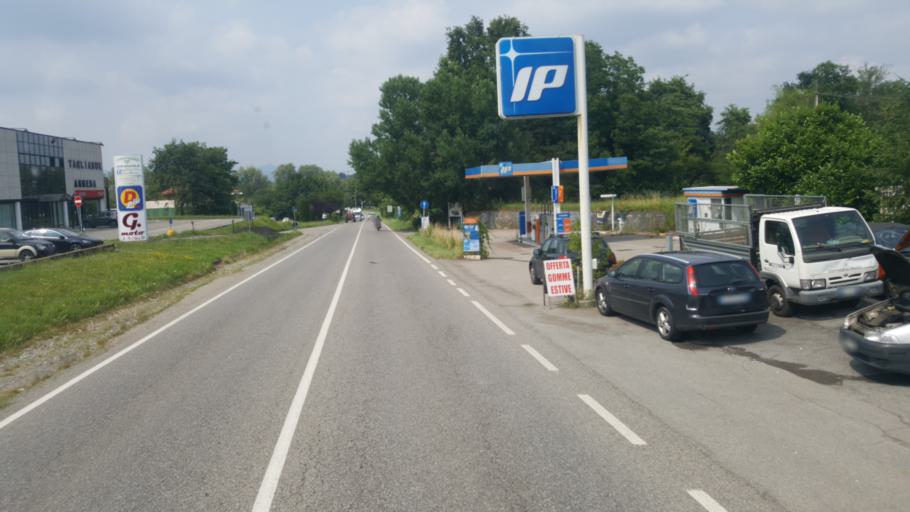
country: IT
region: Lombardy
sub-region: Provincia di Como
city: Beregazzo
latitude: 45.7724
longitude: 8.9614
